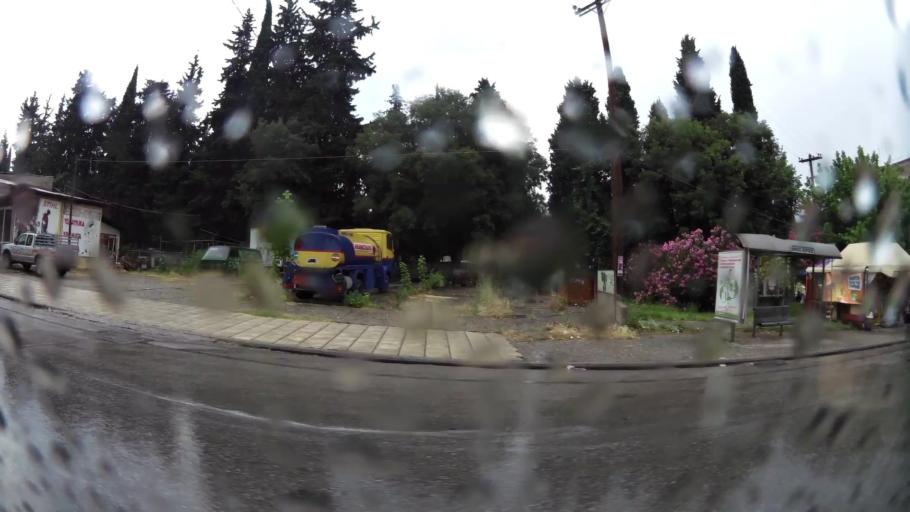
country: GR
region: Central Macedonia
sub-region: Nomos Imathias
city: Veroia
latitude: 40.5331
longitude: 22.2011
